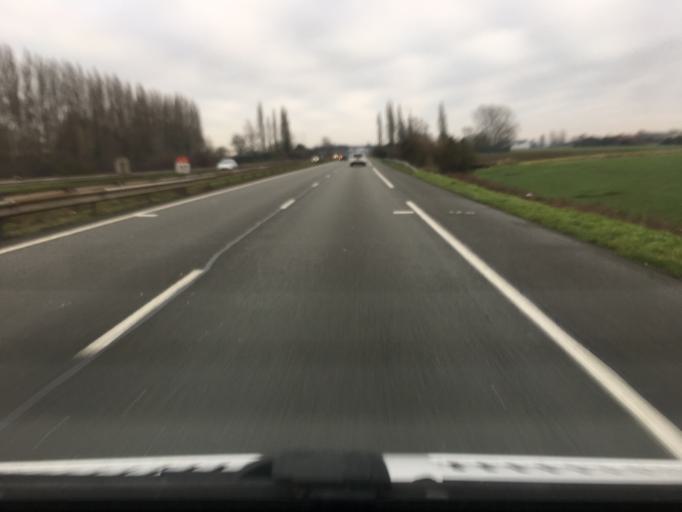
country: FR
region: Nord-Pas-de-Calais
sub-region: Departement du Nord
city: Armentieres
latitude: 50.6673
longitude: 2.8807
